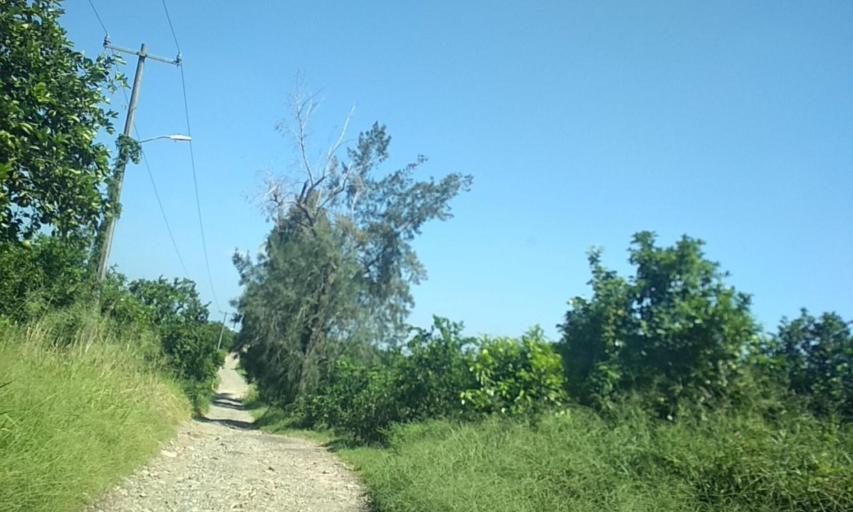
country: MX
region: Veracruz
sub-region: Martinez de la Torre
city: La Union Paso Largo
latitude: 20.1520
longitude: -96.9979
